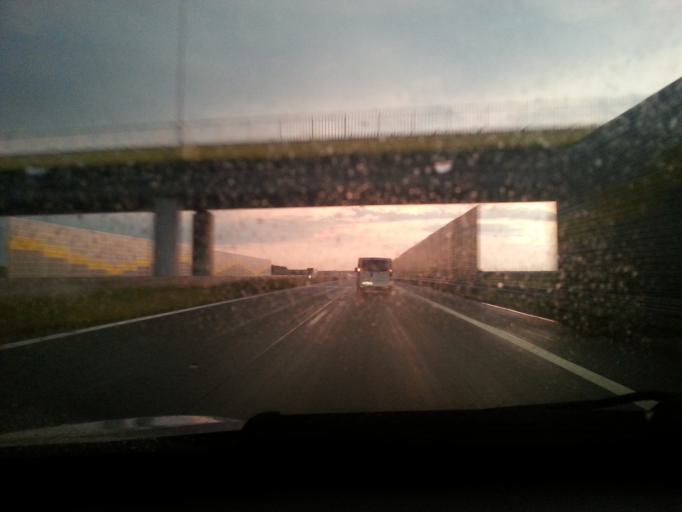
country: PL
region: Lodz Voivodeship
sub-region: Powiat laski
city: Lask
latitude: 51.5631
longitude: 19.1404
